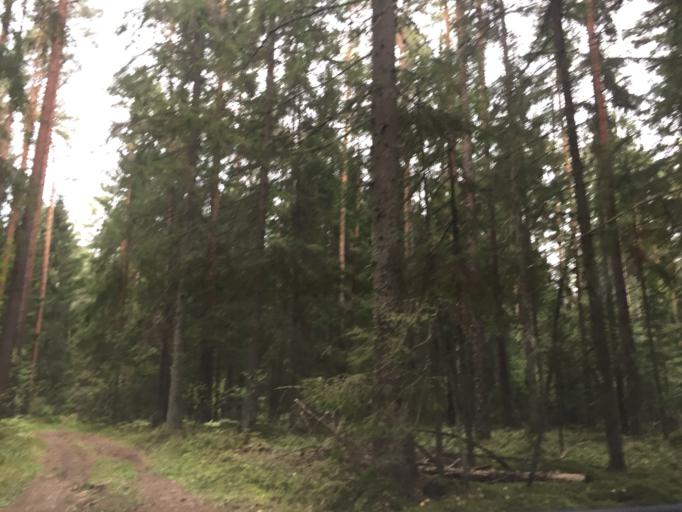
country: LV
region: Baldone
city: Baldone
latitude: 56.7791
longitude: 24.4436
